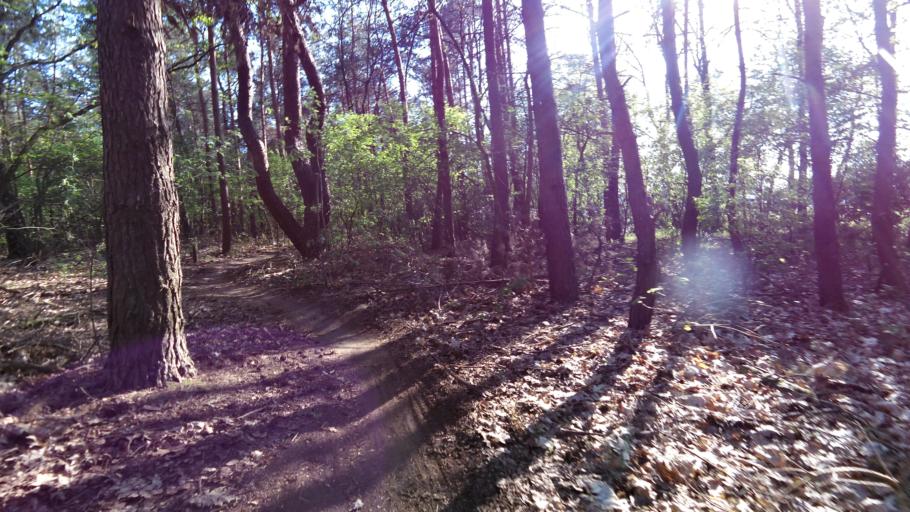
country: NL
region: Gelderland
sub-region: Gemeente Renkum
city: Wolfheze
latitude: 52.0085
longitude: 5.8138
